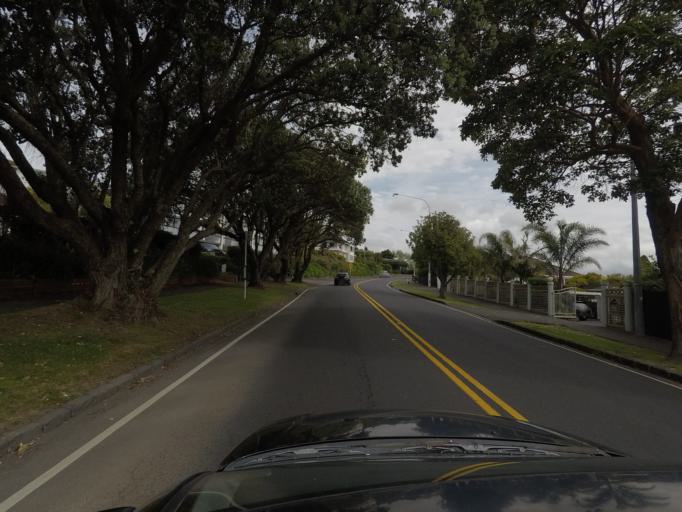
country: NZ
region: Auckland
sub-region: Auckland
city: Auckland
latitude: -36.8569
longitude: 174.8102
